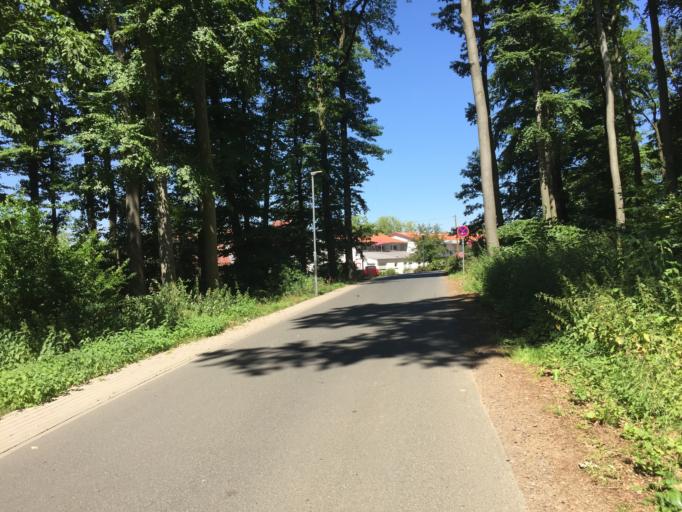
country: DE
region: Hesse
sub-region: Regierungsbezirk Giessen
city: Grossen Buseck
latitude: 50.5960
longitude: 8.8074
